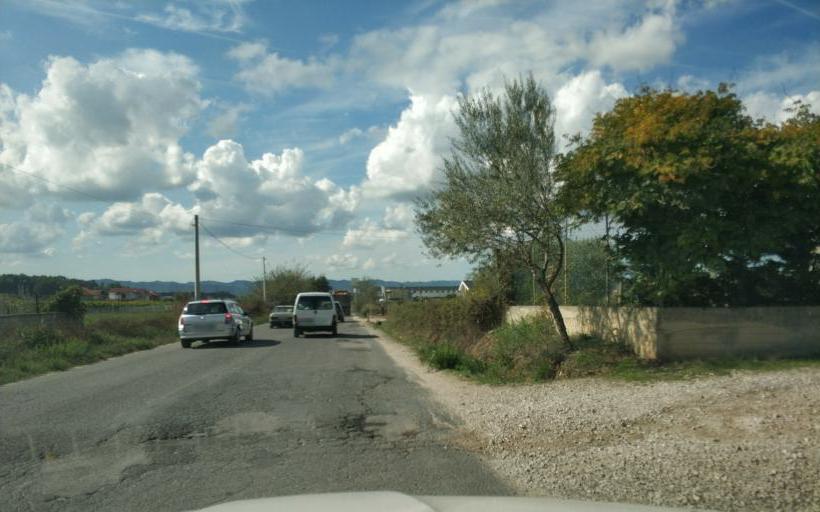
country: AL
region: Durres
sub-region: Rrethi i Krujes
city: Nikel
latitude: 41.4795
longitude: 19.7586
